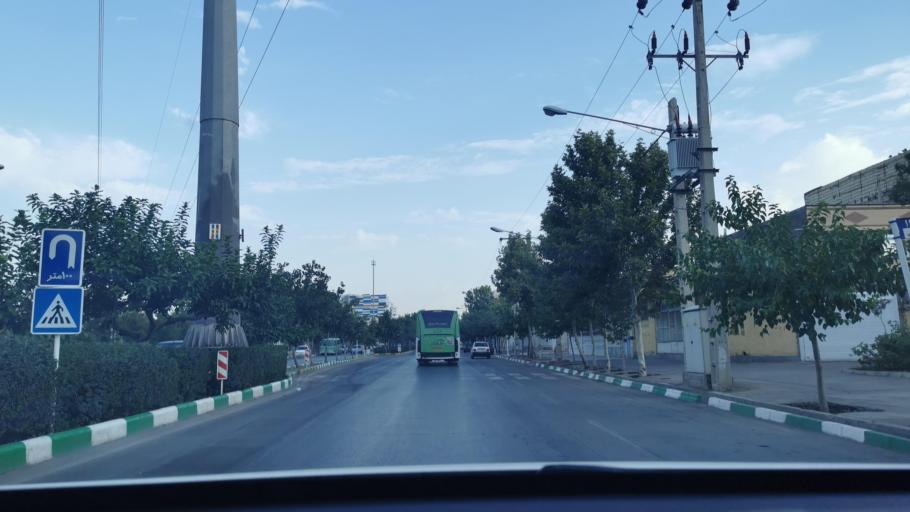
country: IR
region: Razavi Khorasan
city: Mashhad
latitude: 36.3548
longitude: 59.5274
